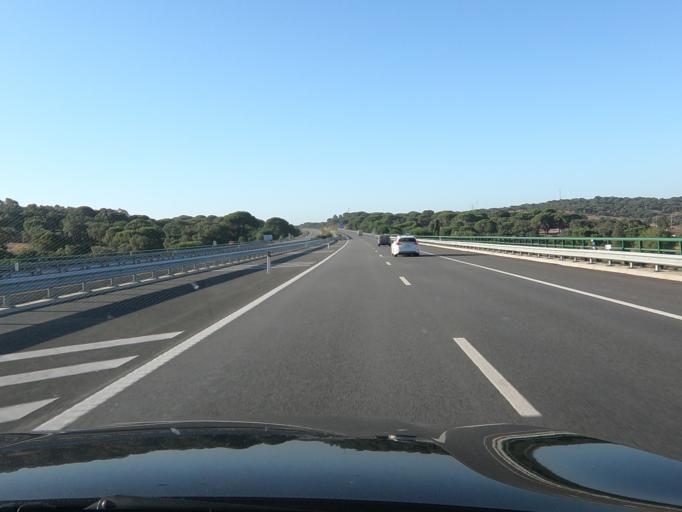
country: PT
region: Setubal
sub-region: Alcacer do Sal
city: Alcacer do Sal
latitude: 38.4345
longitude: -8.5219
